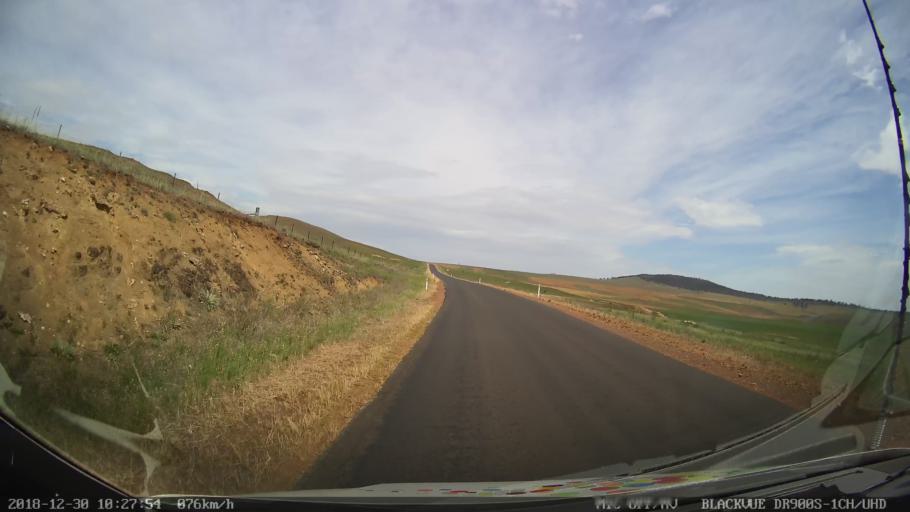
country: AU
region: New South Wales
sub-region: Snowy River
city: Berridale
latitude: -36.5092
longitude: 148.9284
